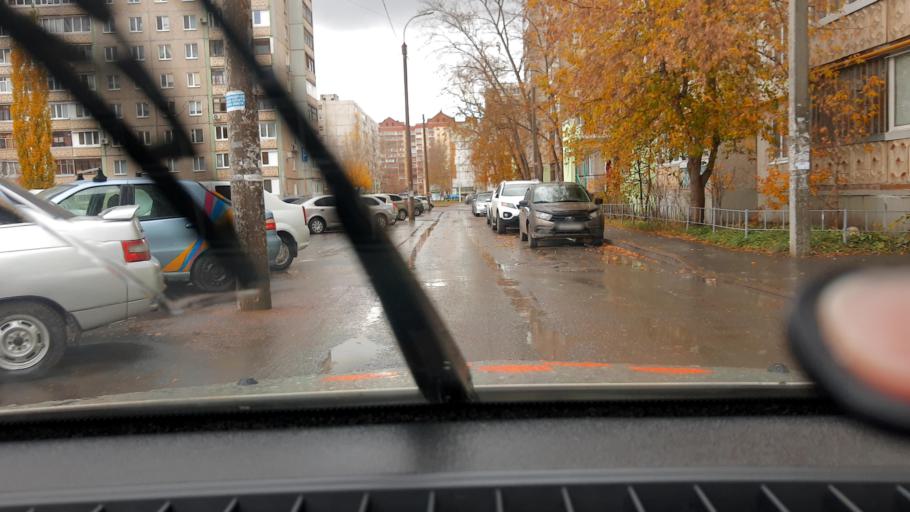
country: RU
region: Bashkortostan
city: Ufa
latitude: 54.7724
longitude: 56.0737
